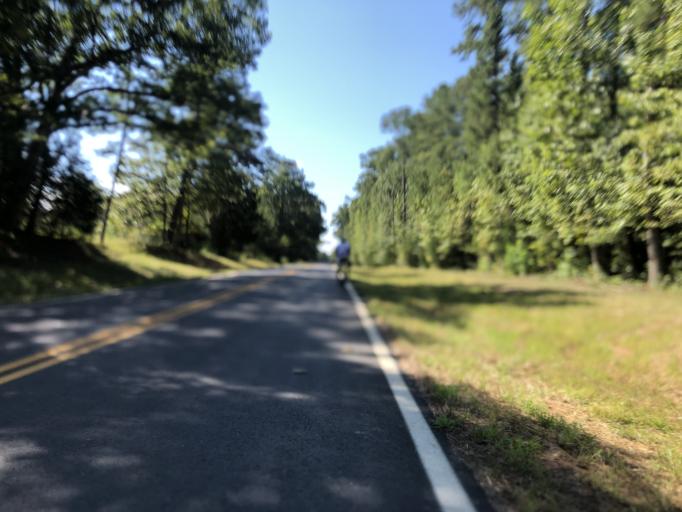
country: US
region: Georgia
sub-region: Heard County
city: Franklin
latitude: 33.3795
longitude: -84.9690
